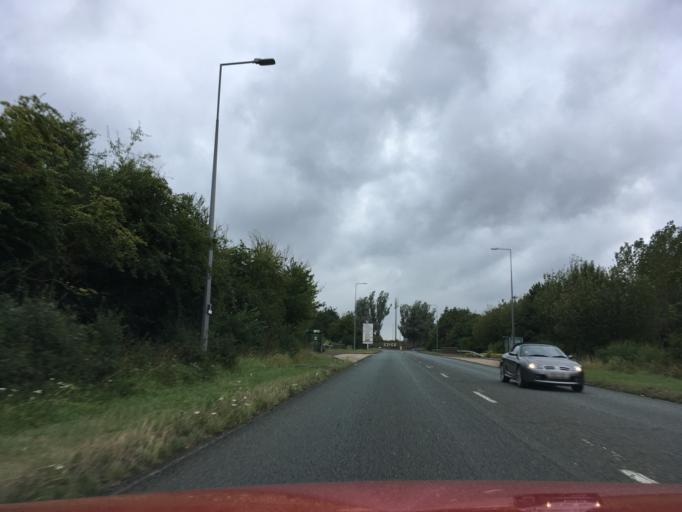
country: GB
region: England
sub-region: Milton Keynes
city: Loughton
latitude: 52.0179
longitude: -0.7650
